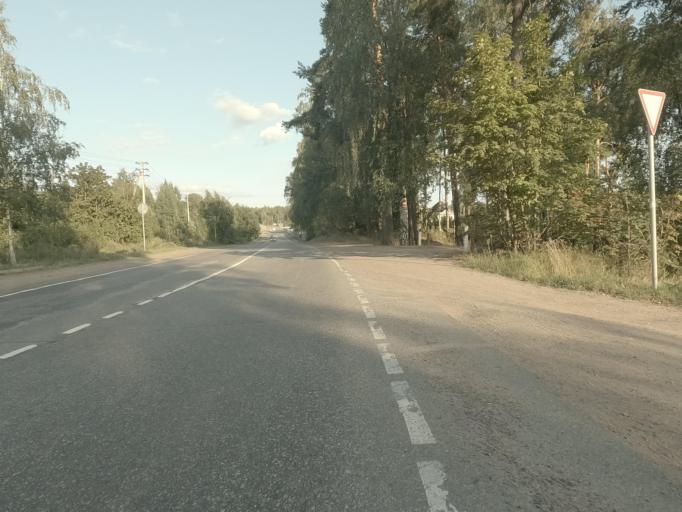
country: RU
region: Leningrad
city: Vyborg
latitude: 60.7263
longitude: 28.7607
